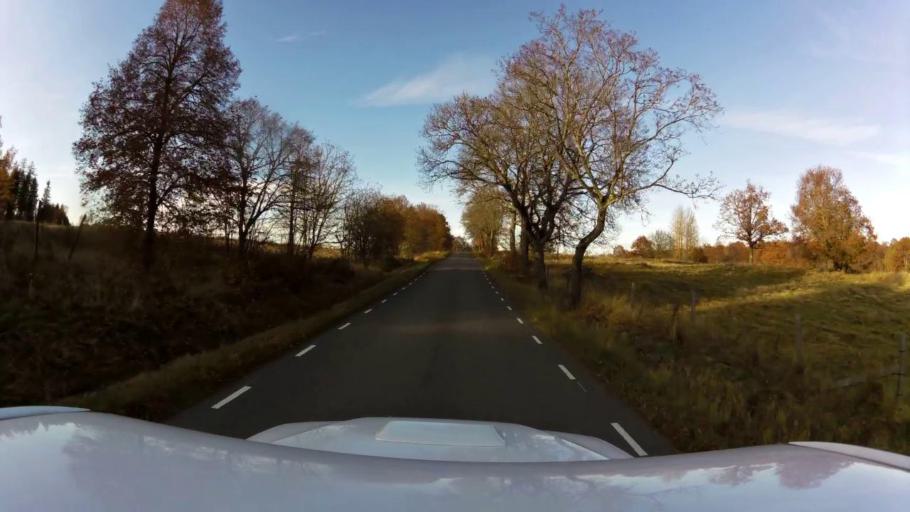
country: SE
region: OEstergoetland
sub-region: Linkopings Kommun
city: Sturefors
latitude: 58.2508
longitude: 15.6631
